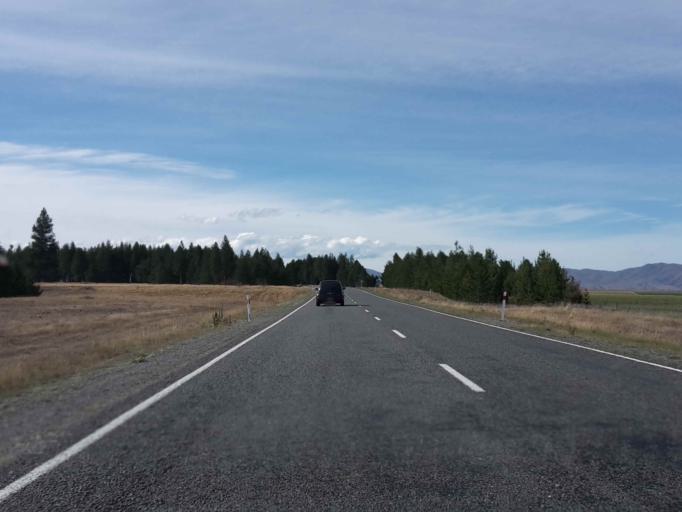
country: NZ
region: Canterbury
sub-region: Timaru District
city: Pleasant Point
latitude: -44.1828
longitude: 170.3126
